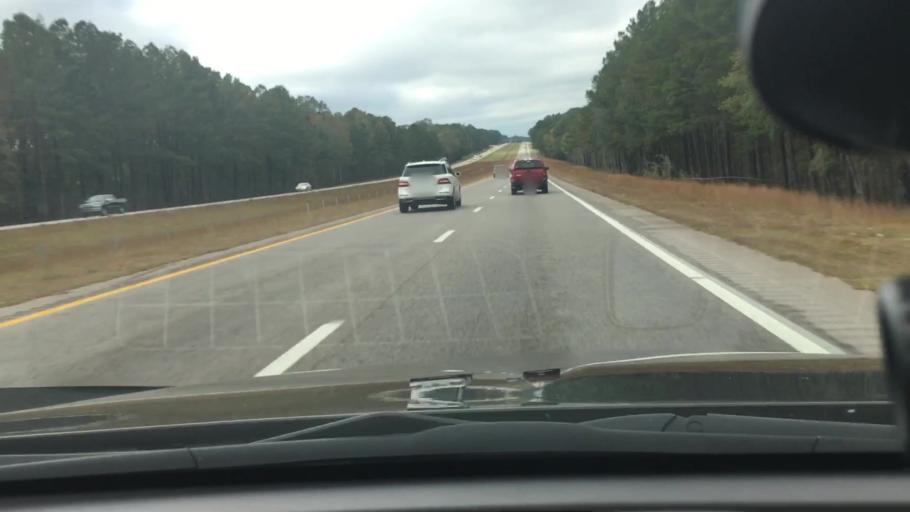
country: US
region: North Carolina
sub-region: Wake County
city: Zebulon
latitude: 35.8167
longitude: -78.2502
